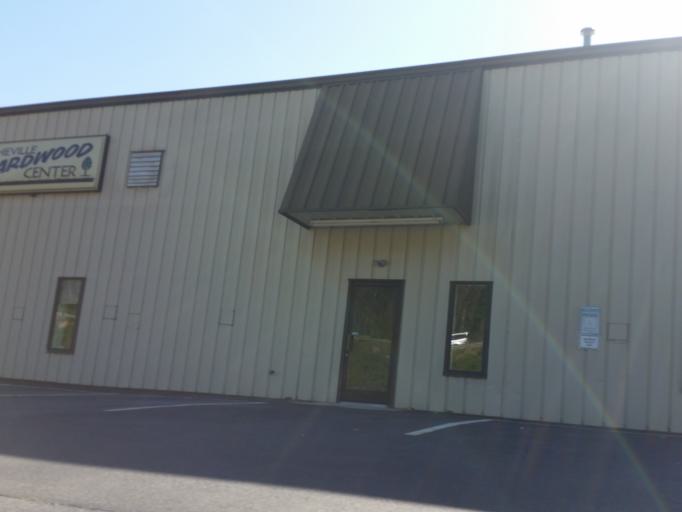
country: US
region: North Carolina
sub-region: Buncombe County
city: Asheville
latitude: 35.6009
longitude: -82.5749
